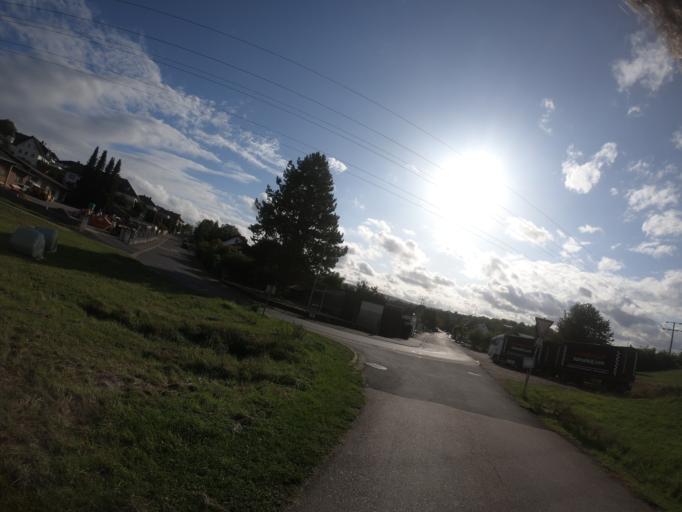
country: DE
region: Hesse
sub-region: Regierungsbezirk Giessen
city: Villmar
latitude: 50.3337
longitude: 8.1833
